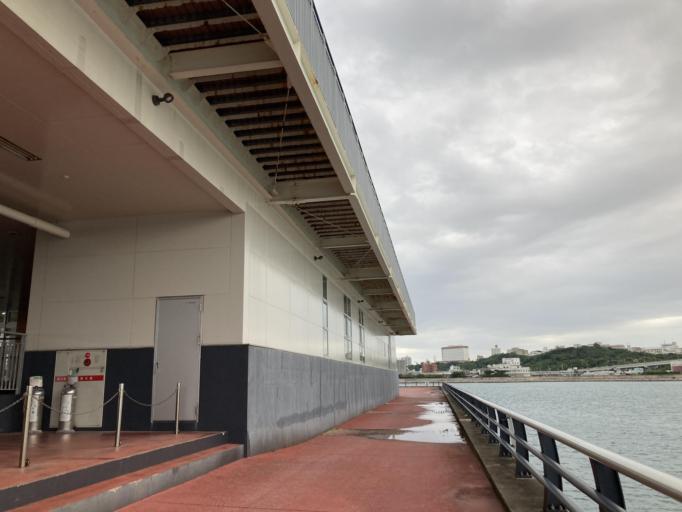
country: JP
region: Okinawa
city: Naha-shi
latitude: 26.2255
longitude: 127.6748
